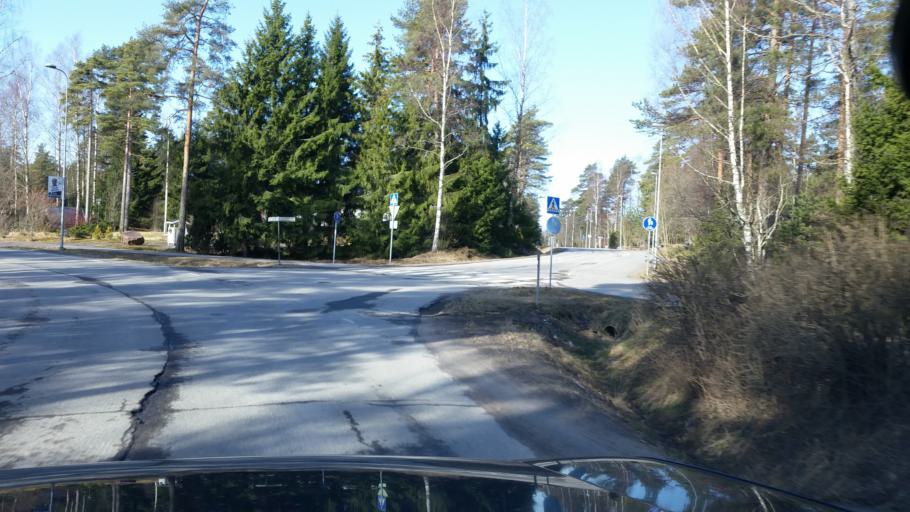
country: FI
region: Uusimaa
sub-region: Raaseporin
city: Inga
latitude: 60.0508
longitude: 24.0155
